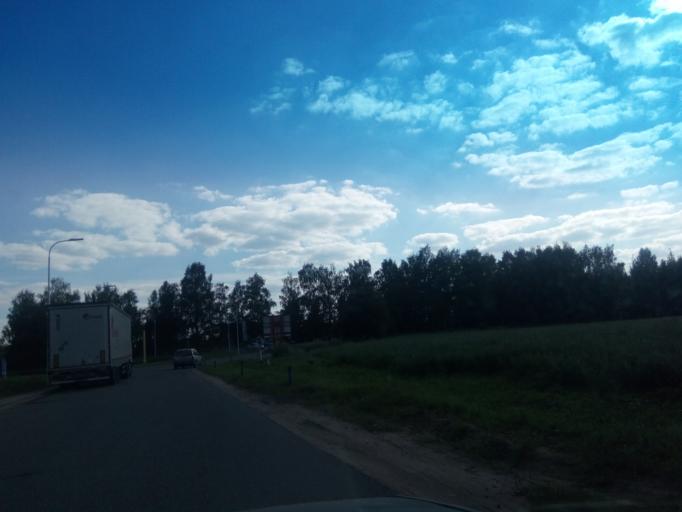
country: BY
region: Vitebsk
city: Navapolatsk
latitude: 55.5436
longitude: 28.6655
